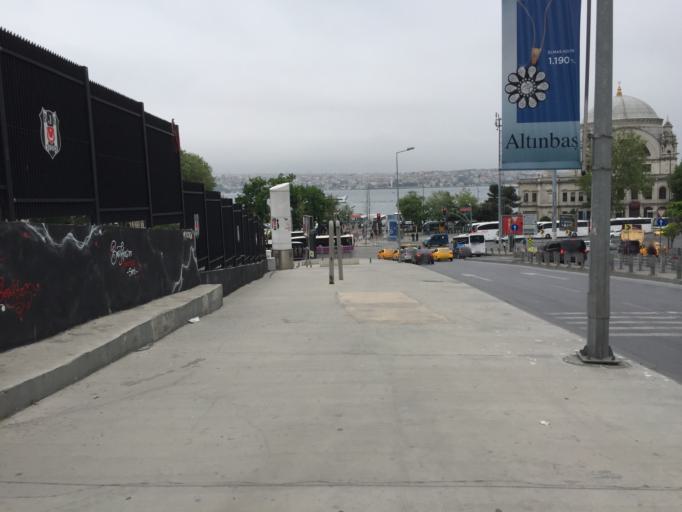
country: TR
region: Istanbul
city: Sisli
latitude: 41.0383
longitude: 28.9944
